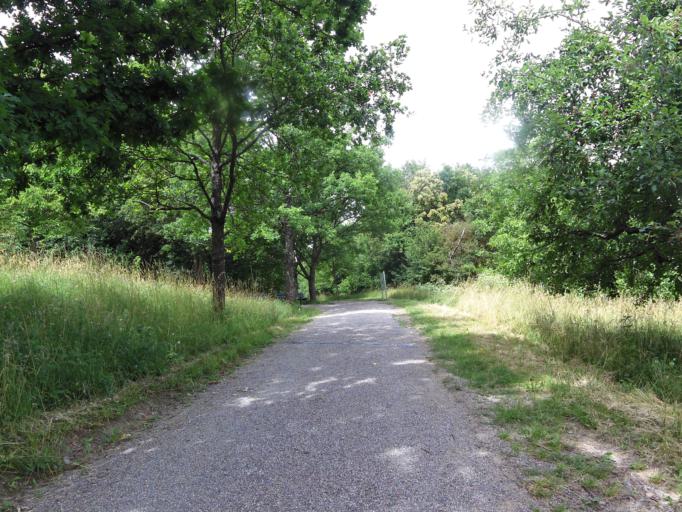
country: DE
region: Bavaria
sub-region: Regierungsbezirk Unterfranken
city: Wuerzburg
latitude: 49.7934
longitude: 9.9713
